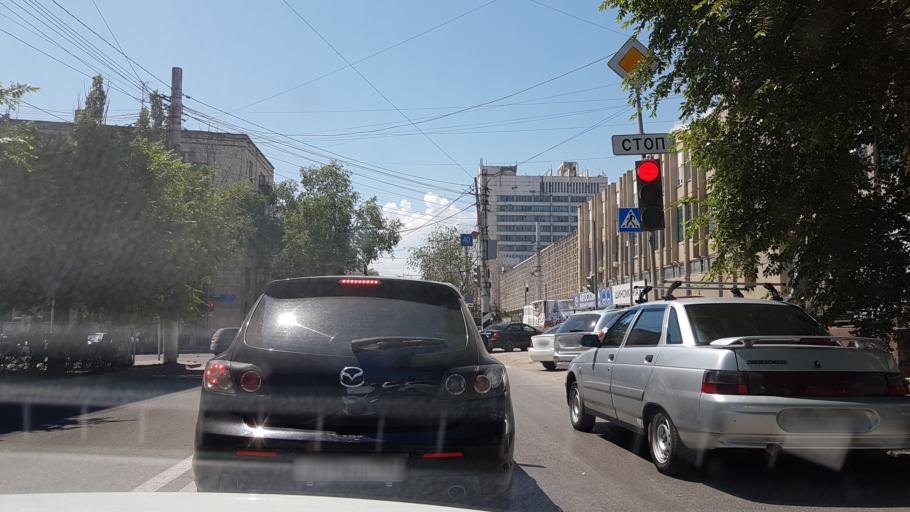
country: RU
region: Volgograd
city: Volgograd
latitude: 48.7139
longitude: 44.5195
